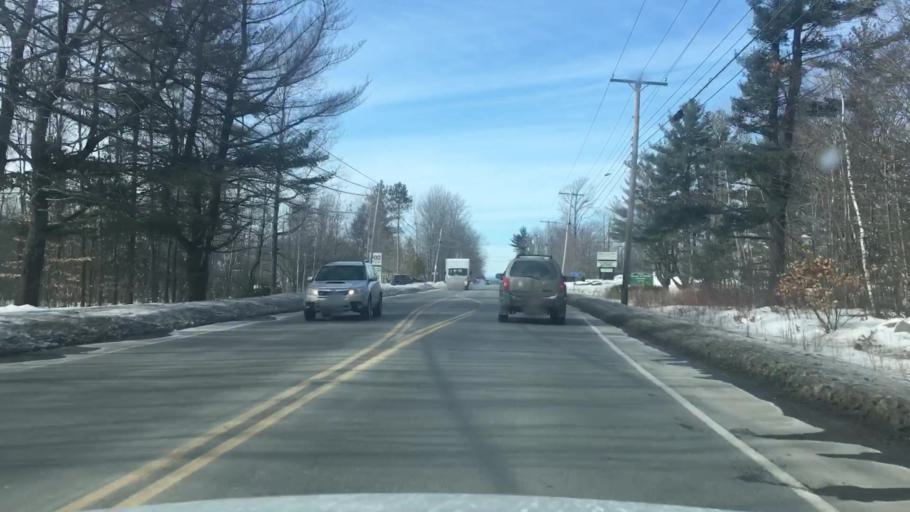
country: US
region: Maine
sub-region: Penobscot County
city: Bangor
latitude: 44.8303
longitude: -68.7858
